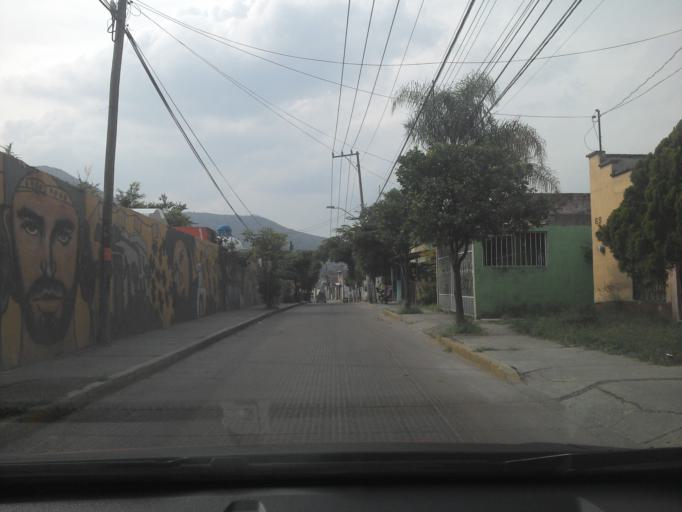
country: MX
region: Jalisco
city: Tlajomulco de Zuniga
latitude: 20.4769
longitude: -103.4430
